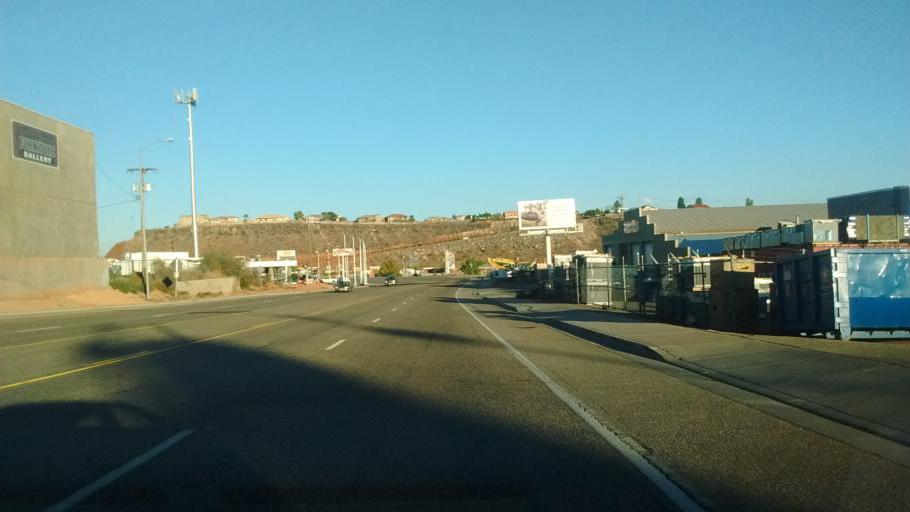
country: US
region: Utah
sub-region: Washington County
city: Saint George
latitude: 37.1129
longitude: -113.5601
